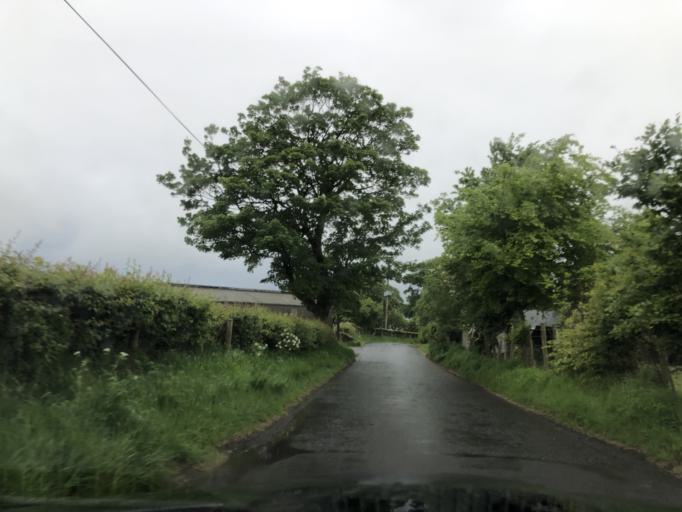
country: GB
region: Northern Ireland
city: Dunloy
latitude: 55.1366
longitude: -6.3718
